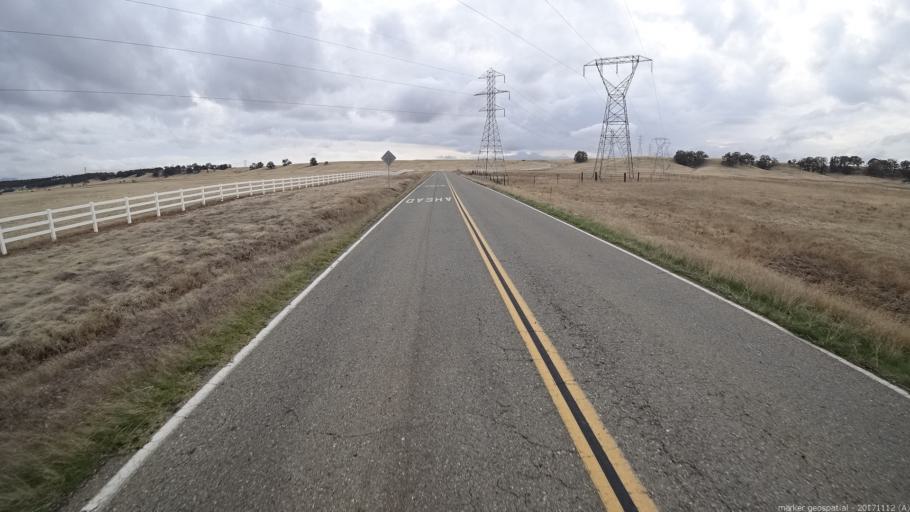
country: US
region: California
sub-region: Shasta County
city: Palo Cedro
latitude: 40.5374
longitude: -122.1741
